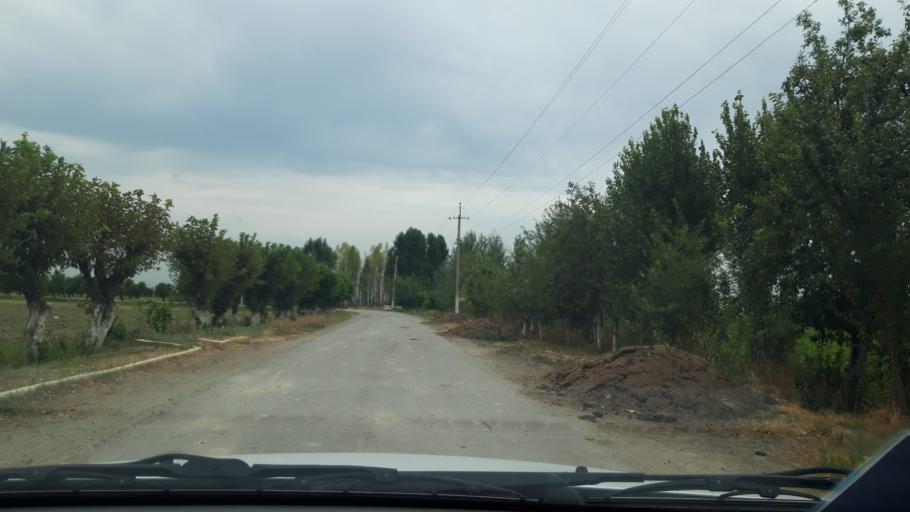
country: UZ
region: Namangan
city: Uychi
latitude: 41.0186
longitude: 71.9186
